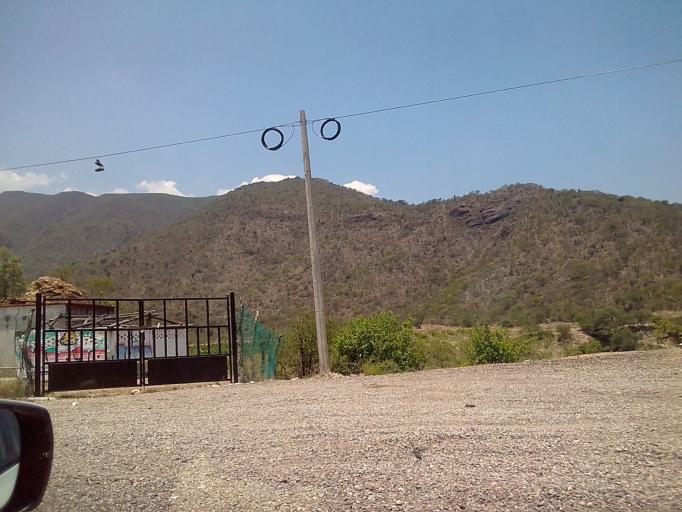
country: MX
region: Oaxaca
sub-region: San Pedro Quiatoni
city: San Pedro Quiatoni
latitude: 16.6759
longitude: -96.1471
